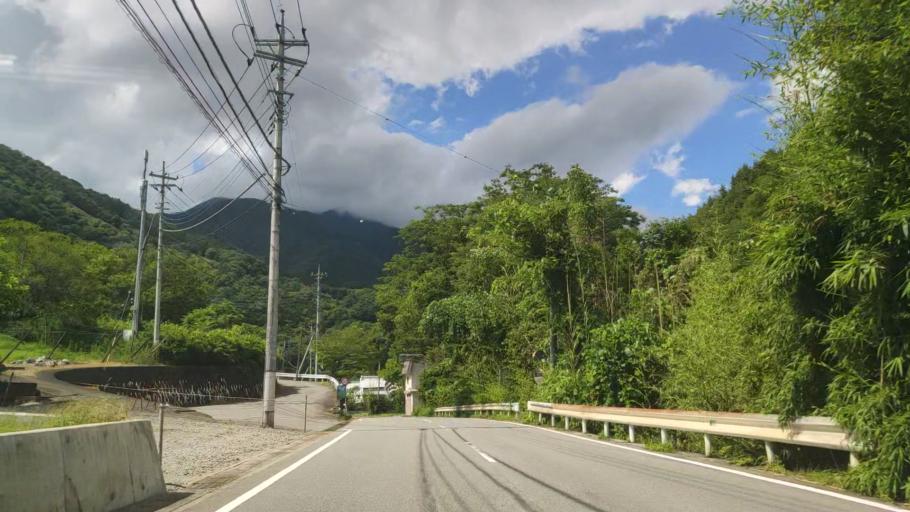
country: JP
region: Yamanashi
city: Enzan
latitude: 35.7834
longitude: 138.7388
